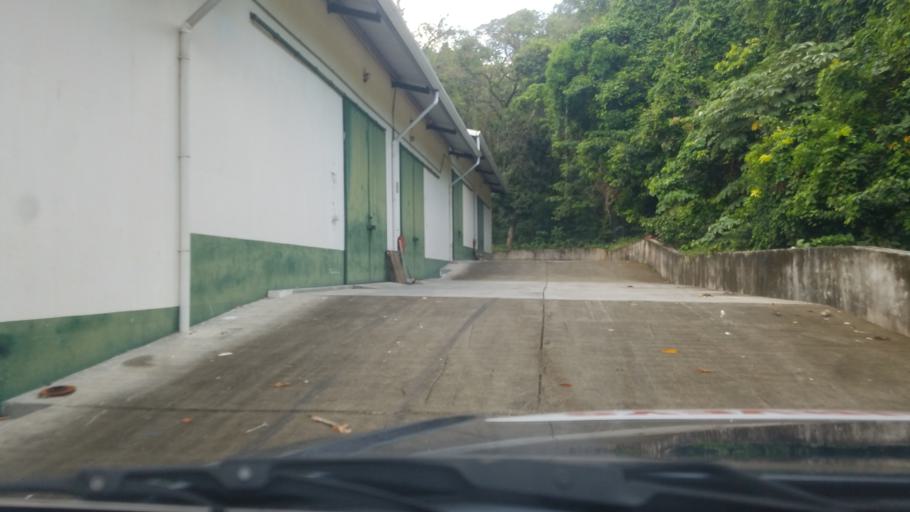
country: LC
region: Castries Quarter
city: Bisee
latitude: 14.0225
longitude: -60.9798
